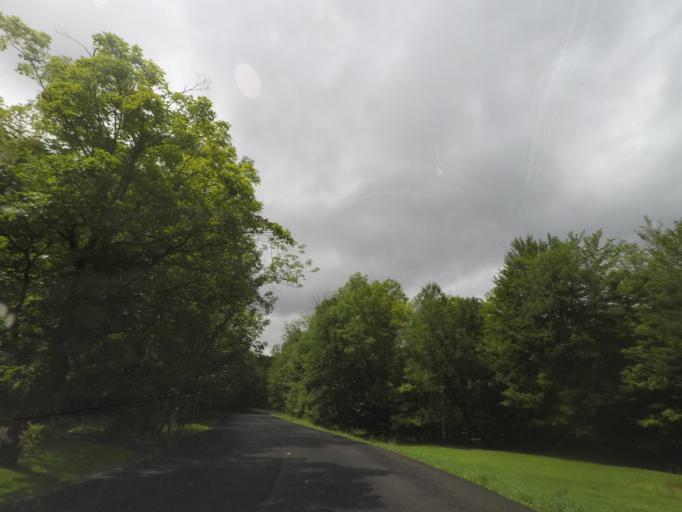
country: US
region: New York
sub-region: Rensselaer County
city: Poestenkill
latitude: 42.6896
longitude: -73.4757
